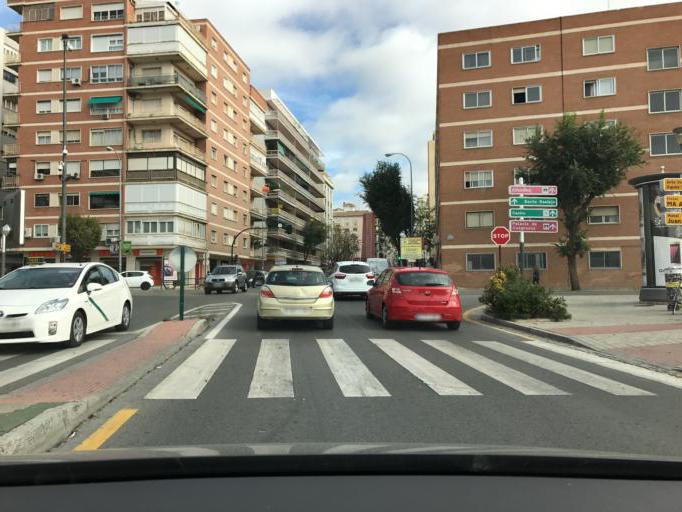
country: ES
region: Andalusia
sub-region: Provincia de Granada
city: Granada
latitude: 37.1692
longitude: -3.6074
